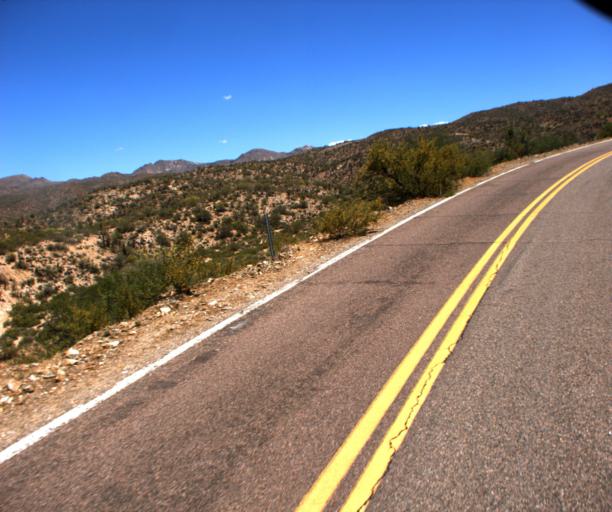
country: US
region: Arizona
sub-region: Yavapai County
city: Bagdad
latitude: 34.4609
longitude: -113.0251
